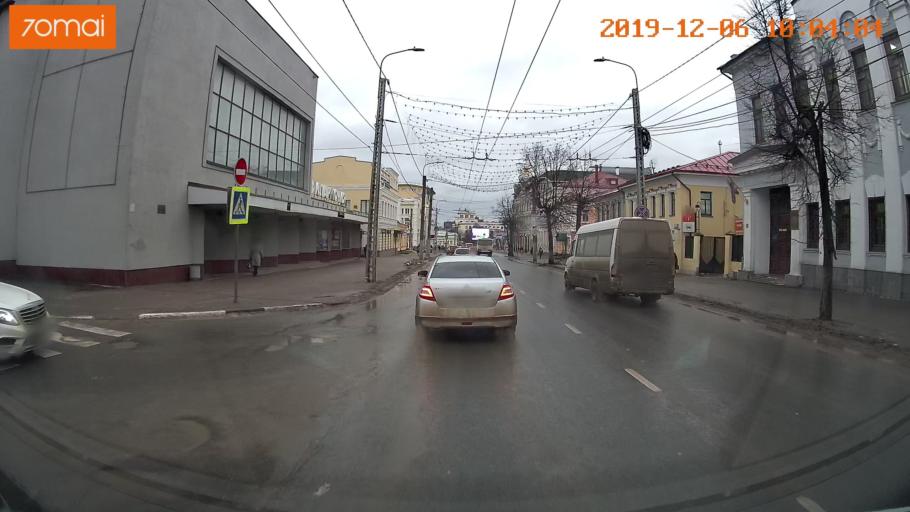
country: RU
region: Ivanovo
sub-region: Gorod Ivanovo
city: Ivanovo
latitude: 56.9945
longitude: 40.9764
